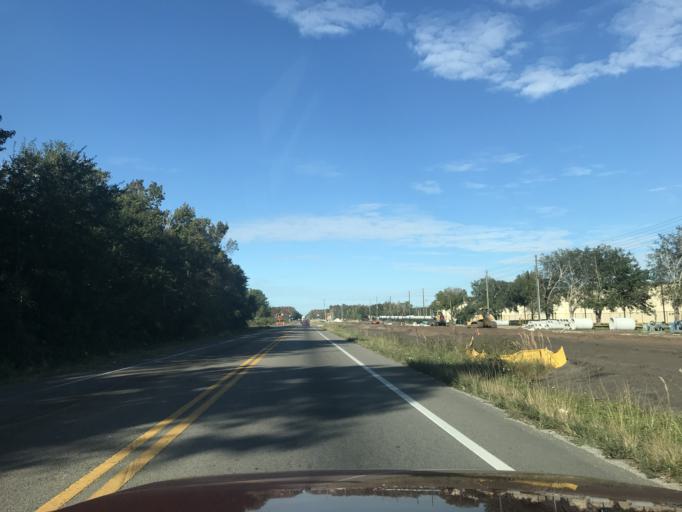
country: US
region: Florida
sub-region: Osceola County
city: Campbell
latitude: 28.2564
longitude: -81.4887
